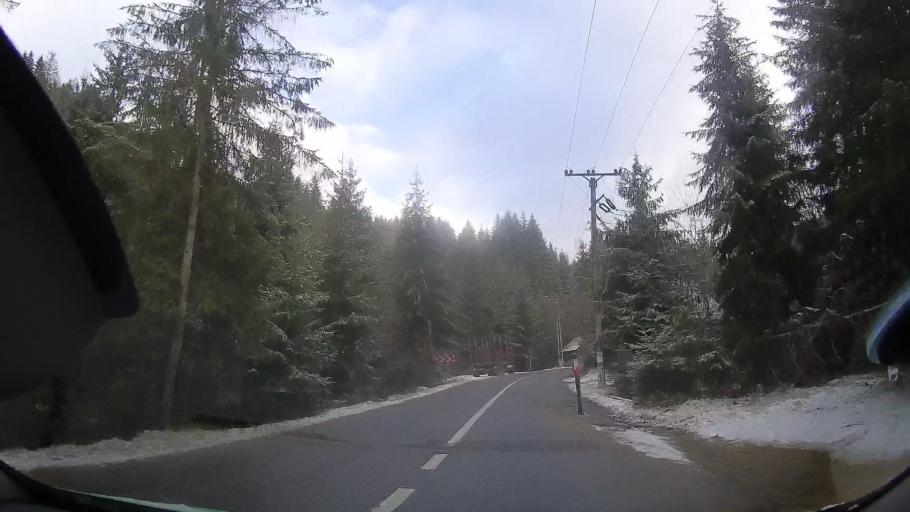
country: RO
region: Alba
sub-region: Comuna Horea
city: Horea
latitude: 46.4870
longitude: 22.9604
